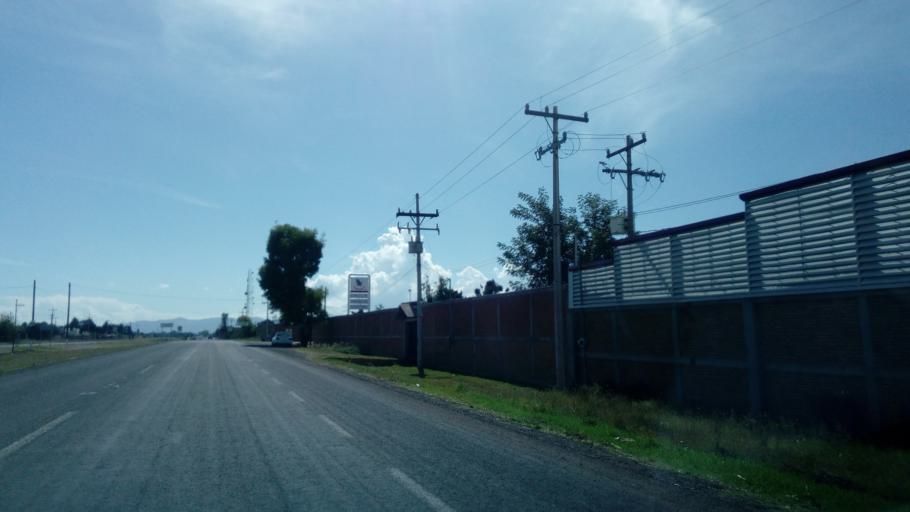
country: MX
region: Durango
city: Victoria de Durango
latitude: 24.0837
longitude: -104.5598
